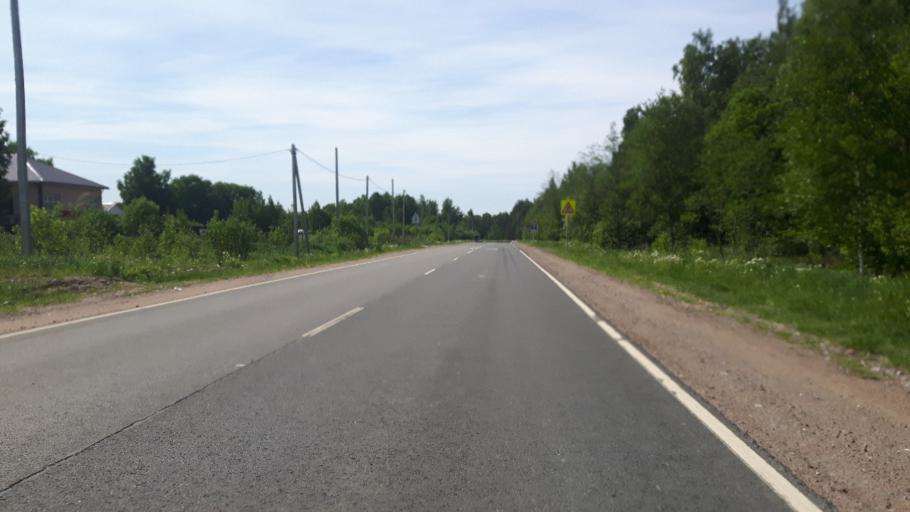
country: RU
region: Leningrad
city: Vistino
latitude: 59.6750
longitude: 28.4510
